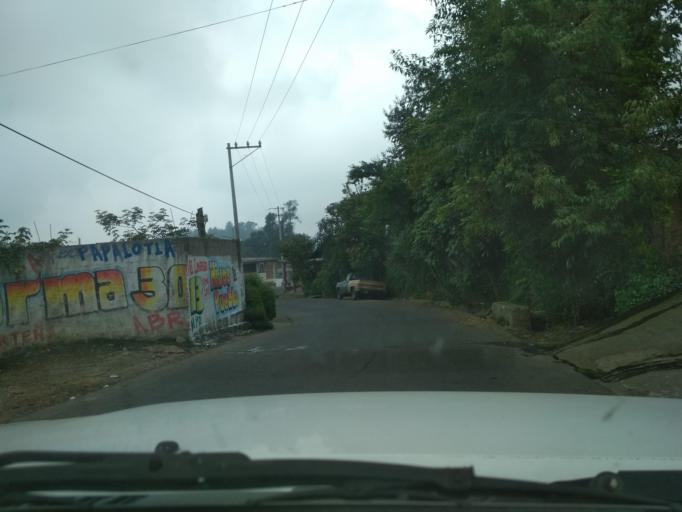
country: MX
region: Veracruz
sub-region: La Perla
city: Metlac Hernandez (Metlac Primero)
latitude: 18.9607
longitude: -97.1585
